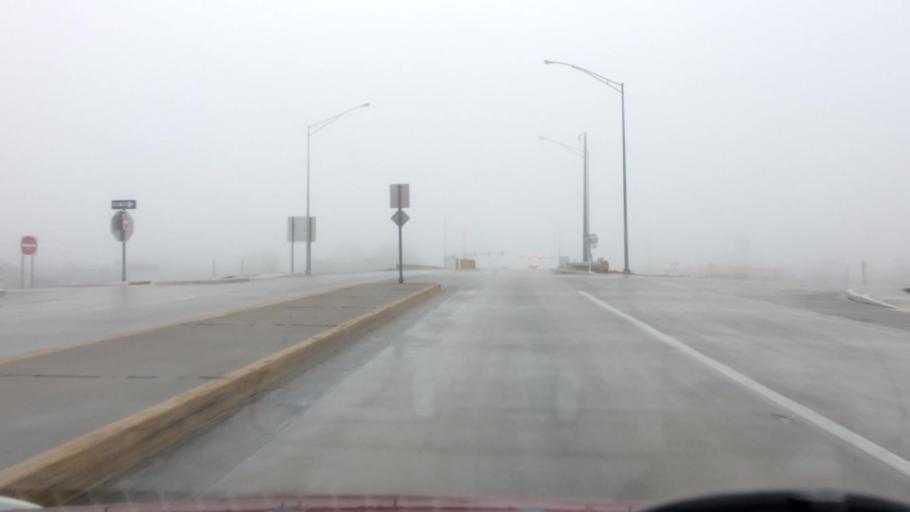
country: US
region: Missouri
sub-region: Greene County
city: Strafford
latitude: 37.2739
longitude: -93.1134
